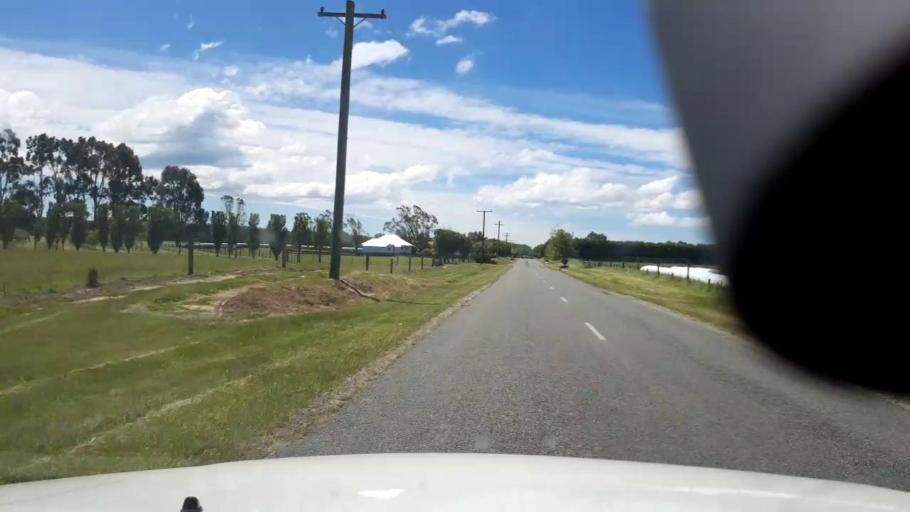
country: NZ
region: Canterbury
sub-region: Timaru District
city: Pleasant Point
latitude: -44.2745
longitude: 171.2531
